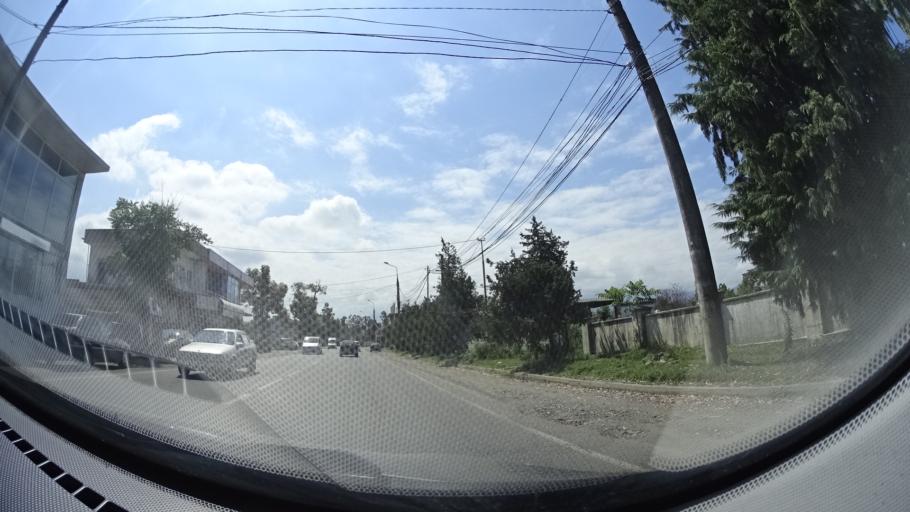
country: GE
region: Ajaria
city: Batumi
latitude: 41.6186
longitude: 41.6181
